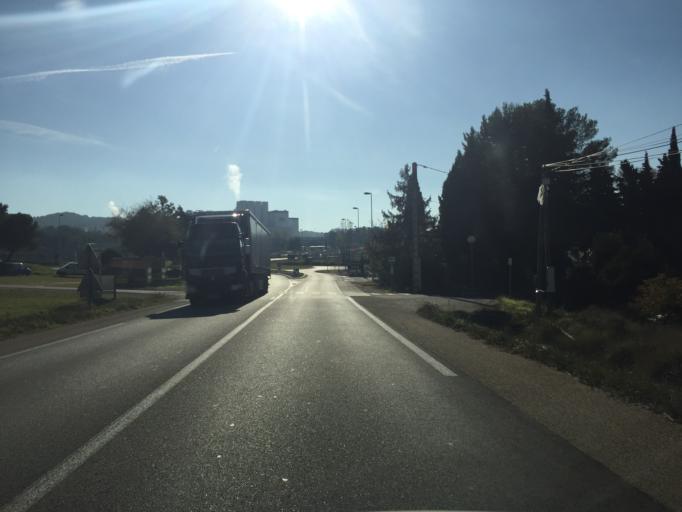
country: FR
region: Provence-Alpes-Cote d'Azur
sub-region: Departement des Bouches-du-Rhone
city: Orgon
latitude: 43.7939
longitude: 5.0292
